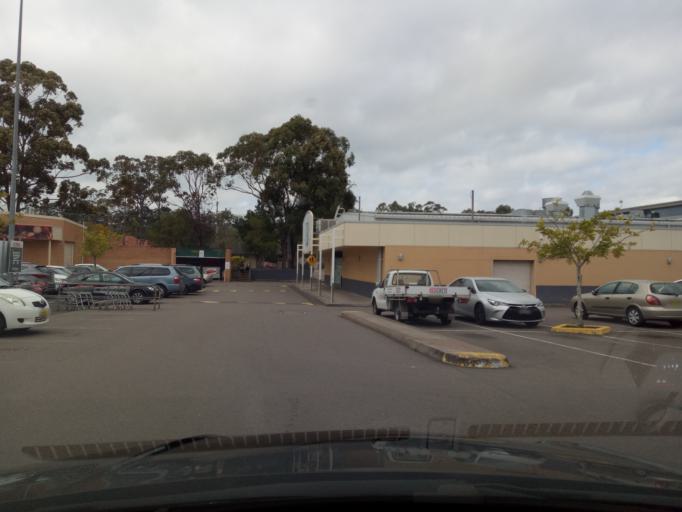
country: AU
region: New South Wales
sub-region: Gosford Shire
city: Narara
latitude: -33.4044
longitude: 151.3523
